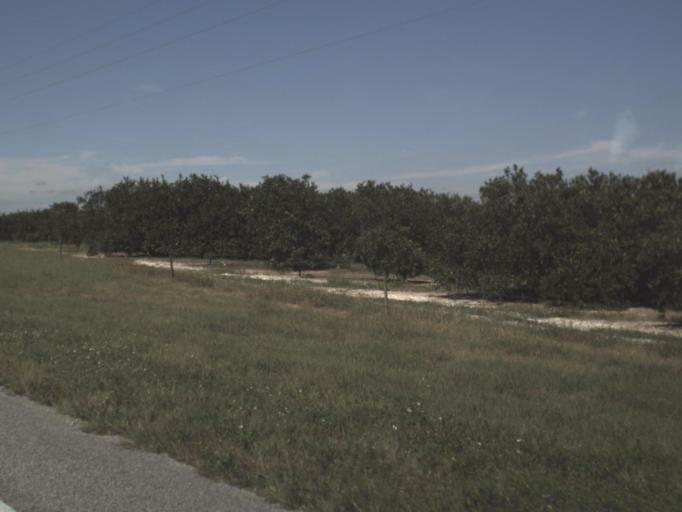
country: US
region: Florida
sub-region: Highlands County
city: Lake Placid
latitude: 27.3592
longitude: -81.3916
